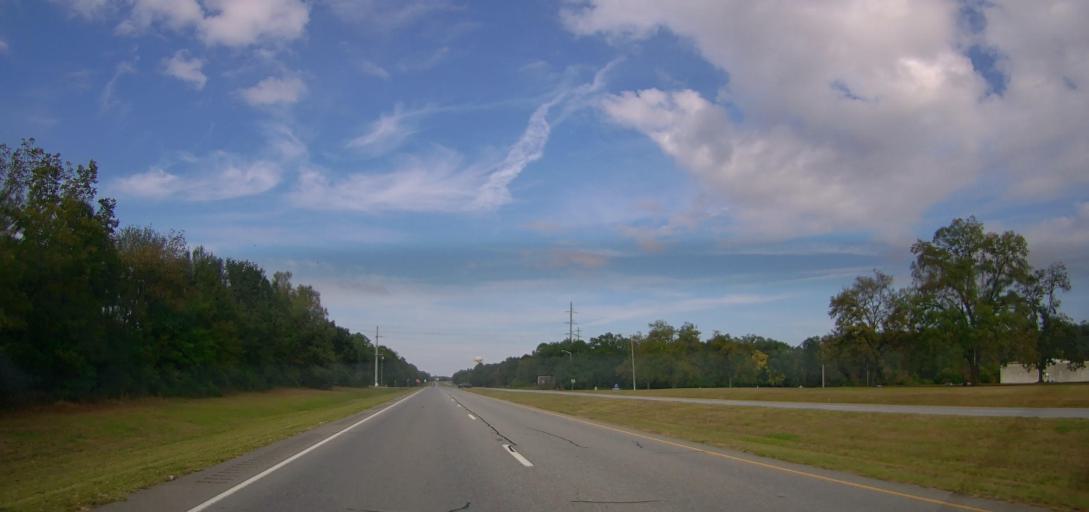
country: US
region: Georgia
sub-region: Mitchell County
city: Camilla
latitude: 31.2594
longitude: -84.1958
